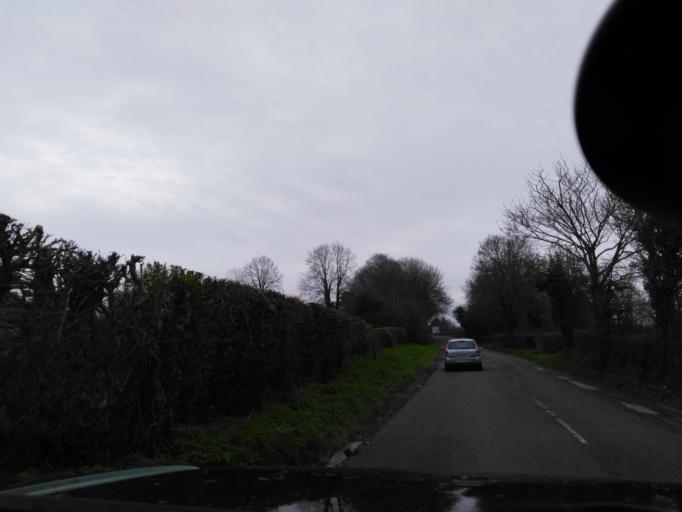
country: GB
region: England
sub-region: Wiltshire
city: Wingfield
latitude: 51.3182
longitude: -2.2580
